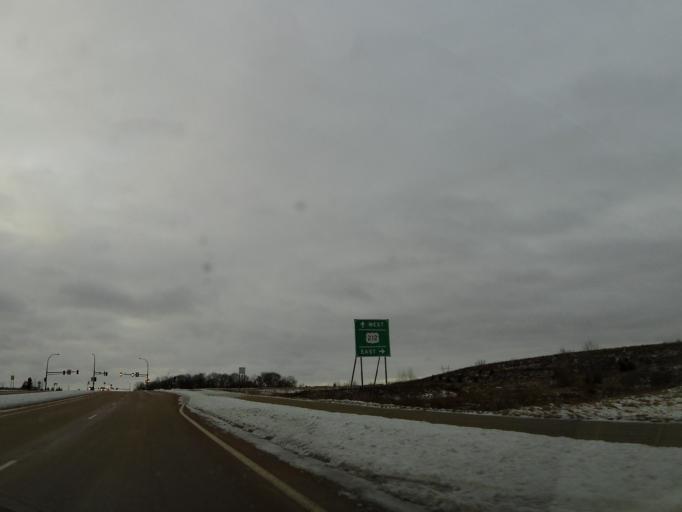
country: US
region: Minnesota
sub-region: Carver County
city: Chaska
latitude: 44.8058
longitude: -93.6215
